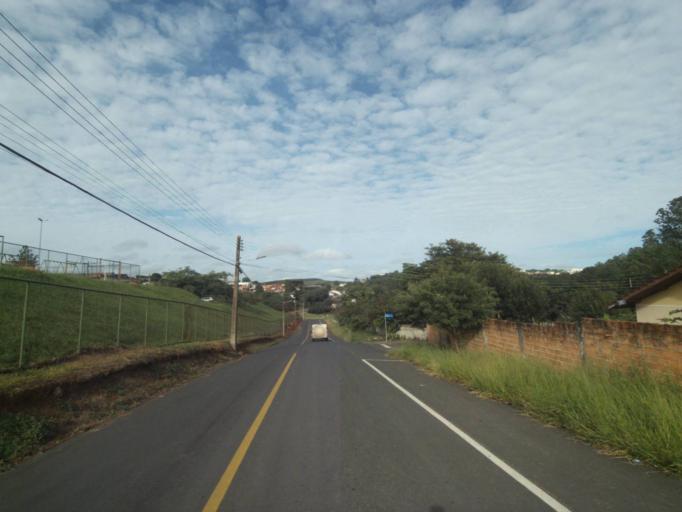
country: BR
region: Parana
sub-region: Telemaco Borba
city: Telemaco Borba
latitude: -24.3434
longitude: -50.6074
